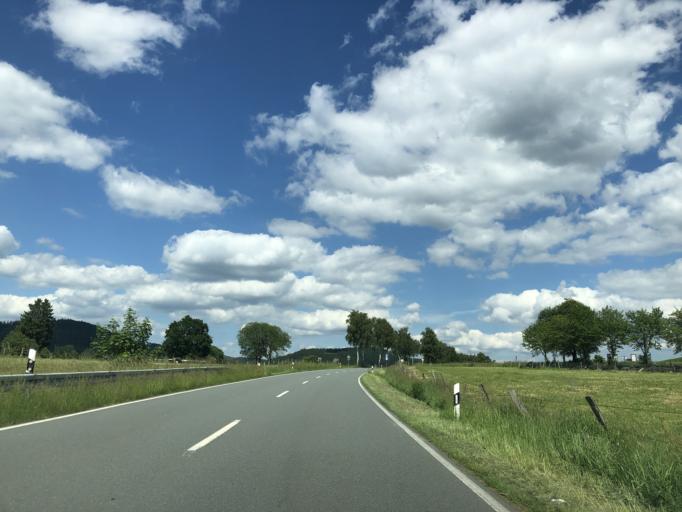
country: DE
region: North Rhine-Westphalia
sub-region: Regierungsbezirk Arnsberg
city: Bad Fredeburg
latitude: 51.1500
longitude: 8.3577
